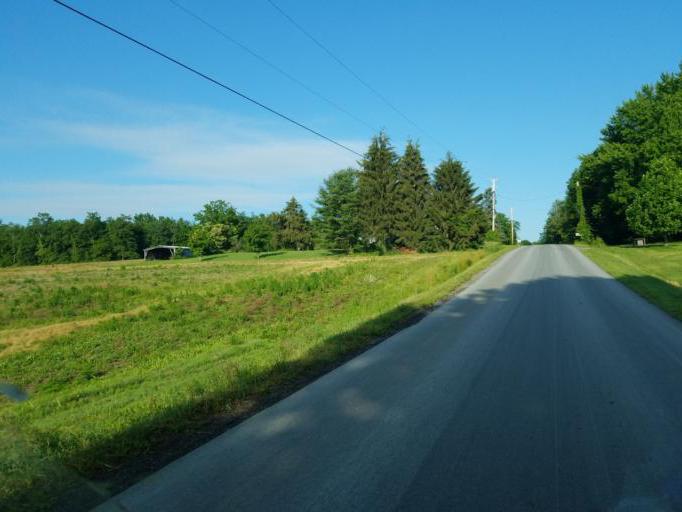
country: US
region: New York
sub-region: Wayne County
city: Clyde
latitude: 43.0453
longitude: -76.8843
